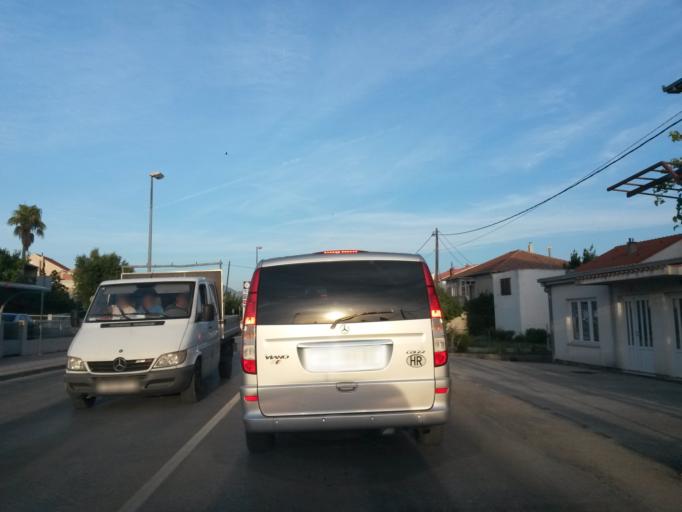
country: HR
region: Splitsko-Dalmatinska
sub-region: Grad Split
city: Split
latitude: 43.5520
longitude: 16.3761
